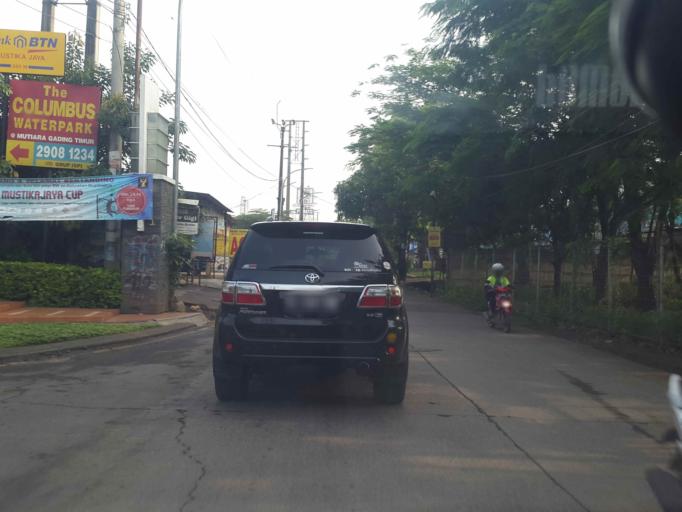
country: ID
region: West Java
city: Bekasi
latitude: -6.2875
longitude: 107.0343
